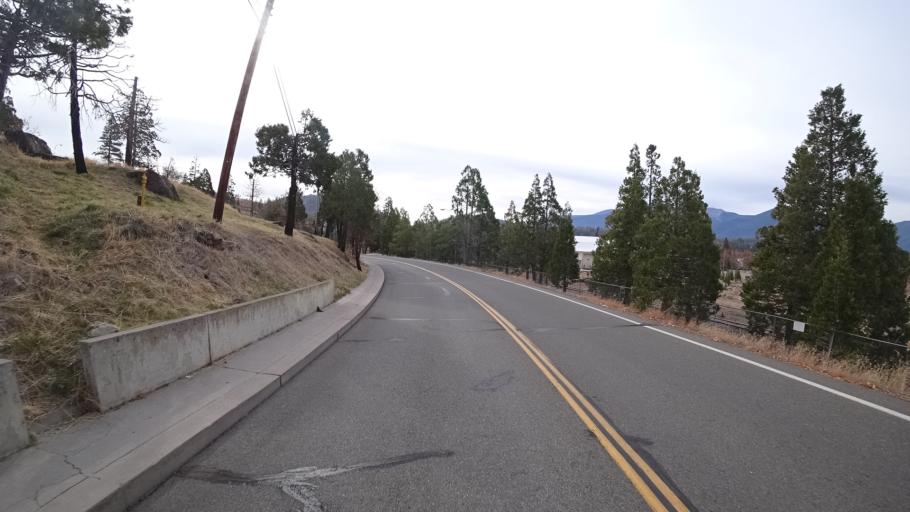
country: US
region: California
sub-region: Siskiyou County
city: Weed
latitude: 41.4296
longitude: -122.3835
